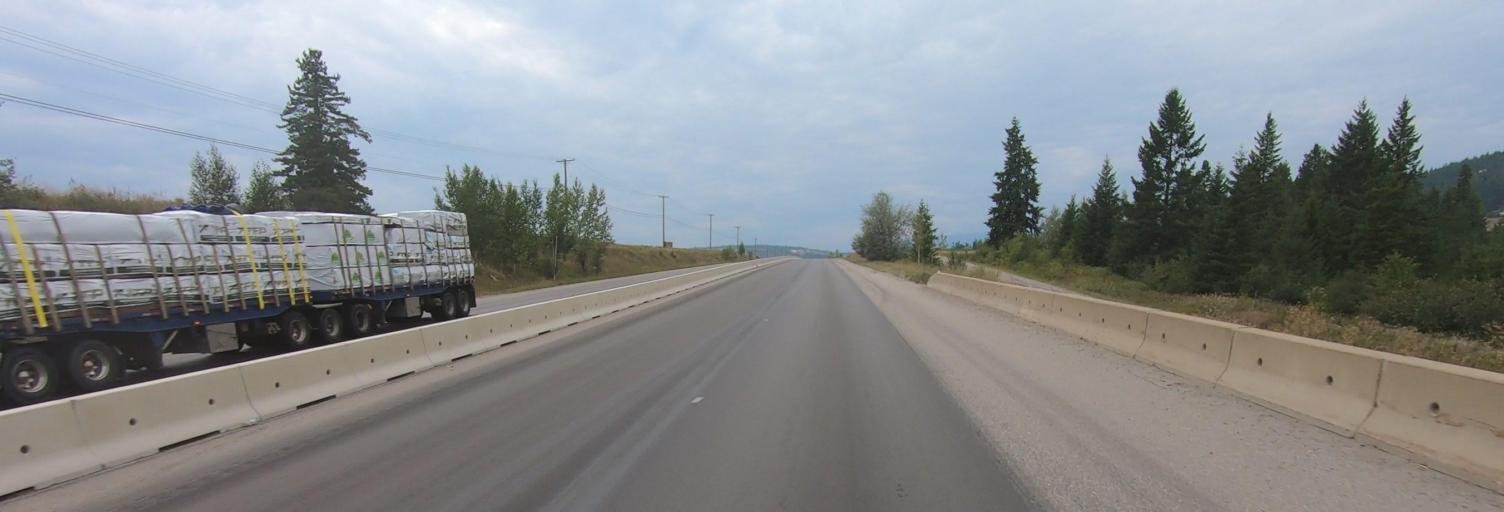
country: CA
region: British Columbia
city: Salmon Arm
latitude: 50.8454
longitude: -119.3335
